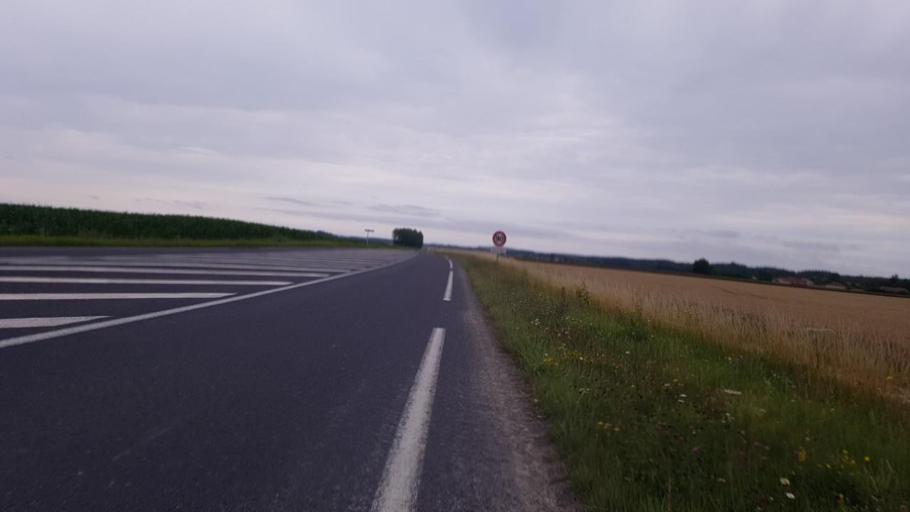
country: FR
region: Champagne-Ardenne
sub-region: Departement de la Marne
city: Pargny-sur-Saulx
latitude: 48.7609
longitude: 4.7808
